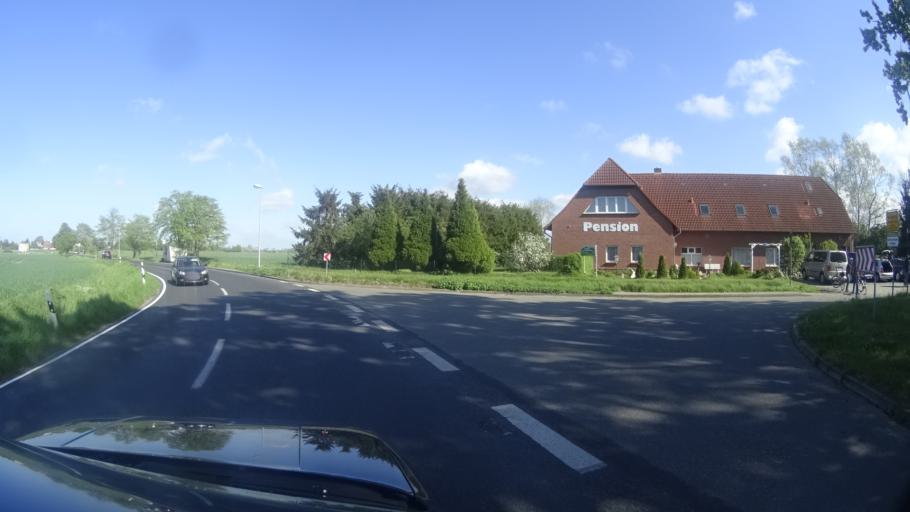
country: DE
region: Mecklenburg-Vorpommern
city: Gelbensande
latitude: 54.2379
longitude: 12.3212
